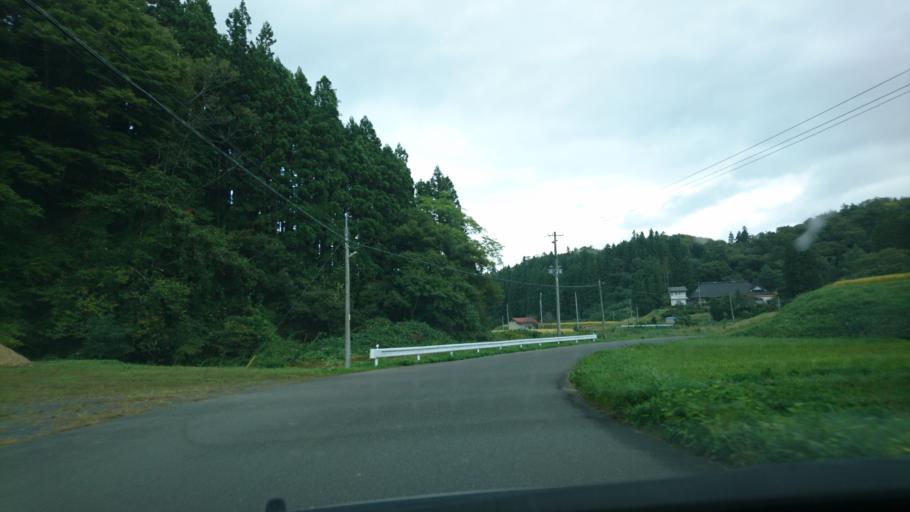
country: JP
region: Iwate
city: Ichinoseki
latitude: 38.9054
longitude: 141.0812
